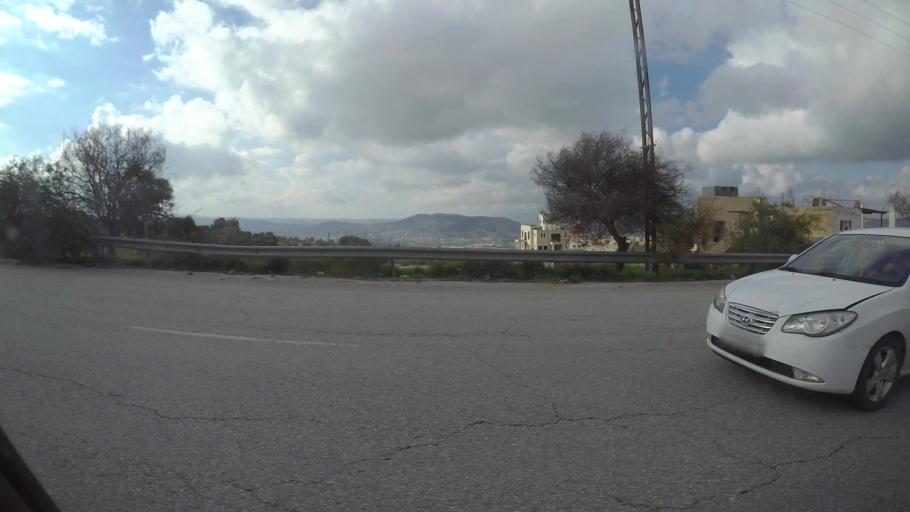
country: JO
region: Amman
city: Al Jubayhah
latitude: 32.0676
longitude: 35.8722
